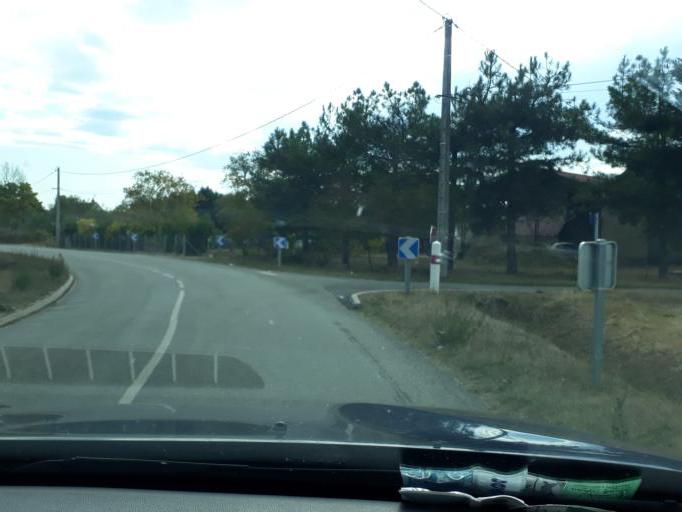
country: FR
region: Centre
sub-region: Departement du Loiret
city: Saint-Benoit-sur-Loire
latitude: 47.8344
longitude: 2.3158
